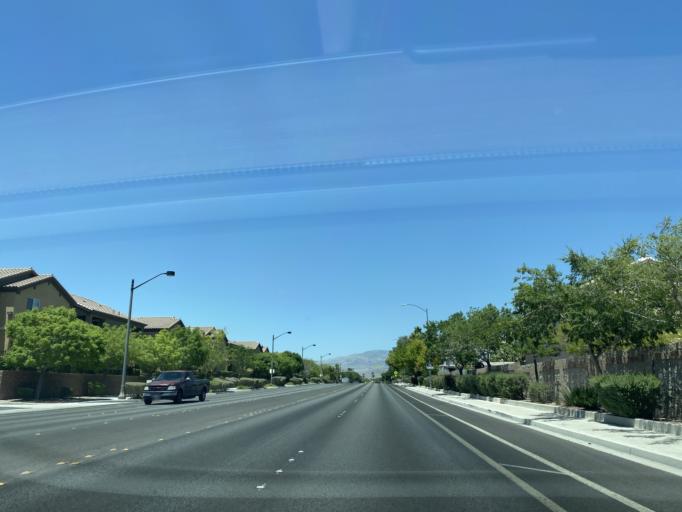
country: US
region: Nevada
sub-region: Clark County
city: Las Vegas
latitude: 36.2858
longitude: -115.2695
